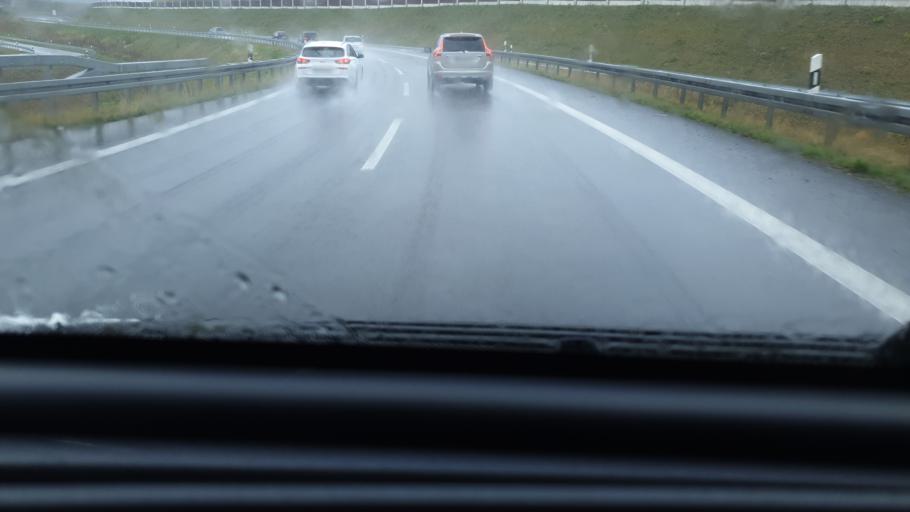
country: DE
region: North Rhine-Westphalia
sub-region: Regierungsbezirk Koln
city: Titz
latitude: 51.0315
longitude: 6.4701
